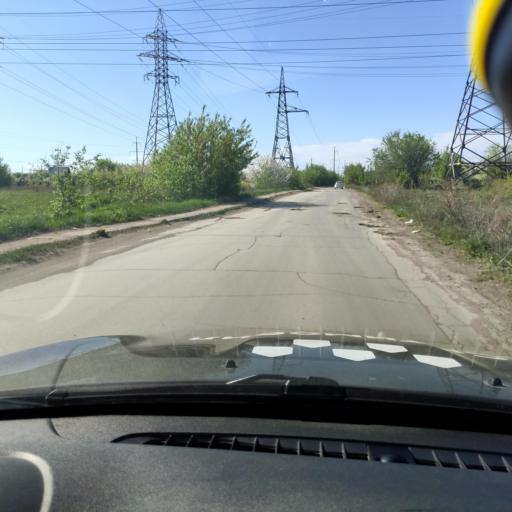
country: RU
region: Samara
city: Tol'yatti
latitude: 53.5887
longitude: 49.2957
